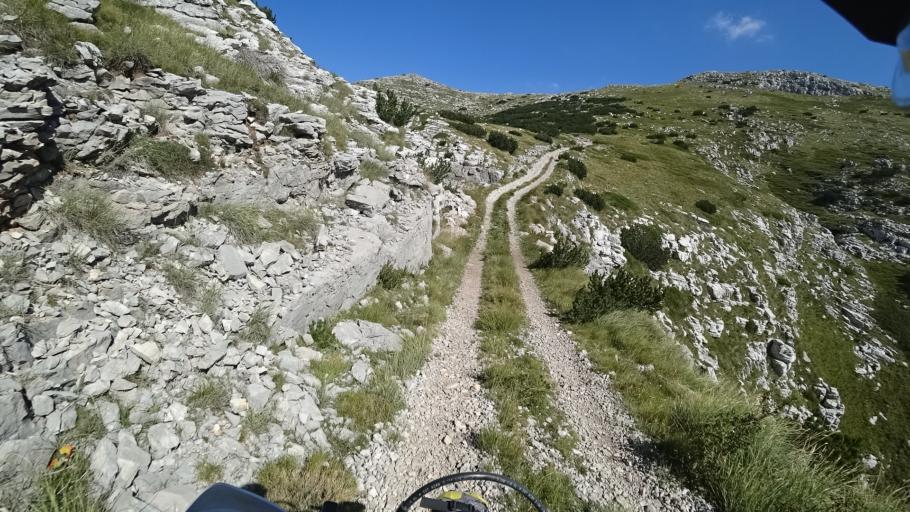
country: HR
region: Splitsko-Dalmatinska
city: Hrvace
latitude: 43.9323
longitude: 16.6007
